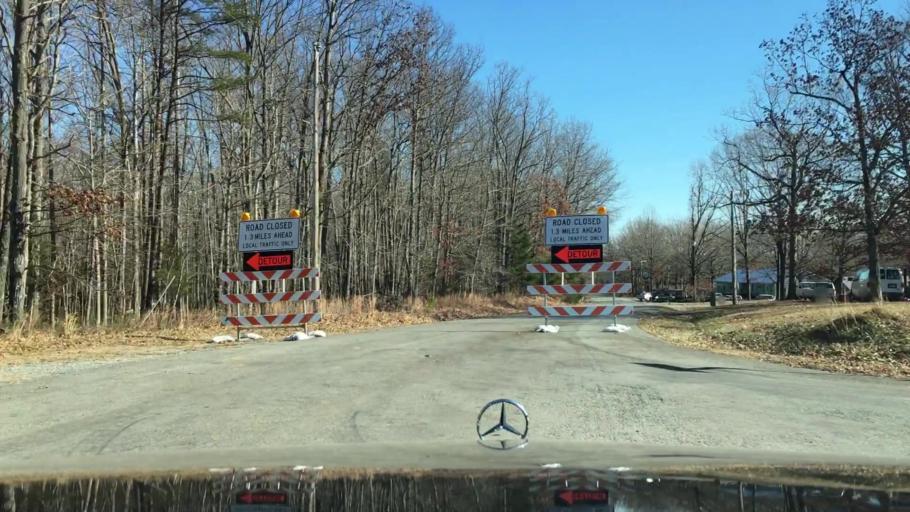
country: US
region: Virginia
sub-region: Campbell County
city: Altavista
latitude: 37.1822
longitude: -79.3198
